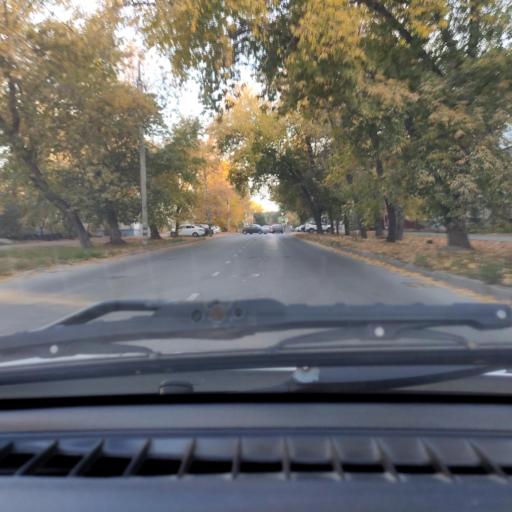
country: RU
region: Samara
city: Tol'yatti
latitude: 53.5058
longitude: 49.4077
